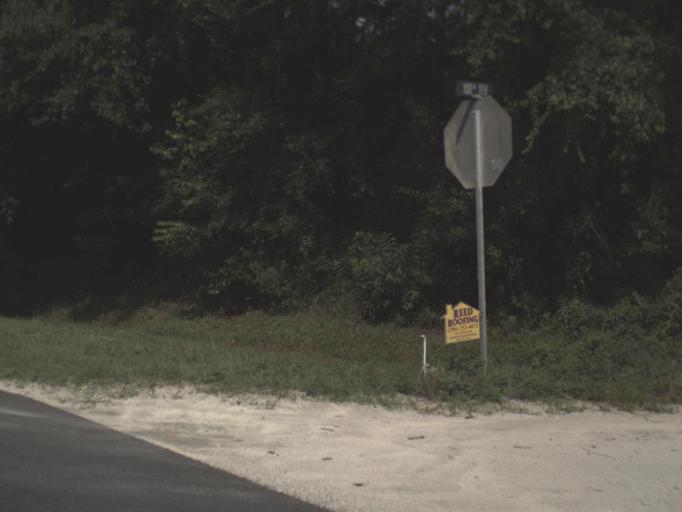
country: US
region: Florida
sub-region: Suwannee County
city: Live Oak
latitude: 30.2659
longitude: -83.0242
